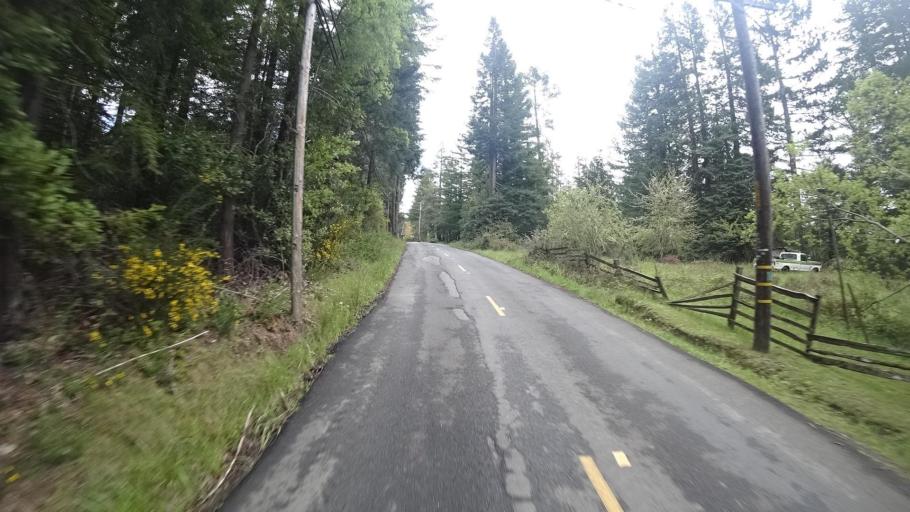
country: US
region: California
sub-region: Humboldt County
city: Bayside
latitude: 40.7859
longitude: -124.0143
